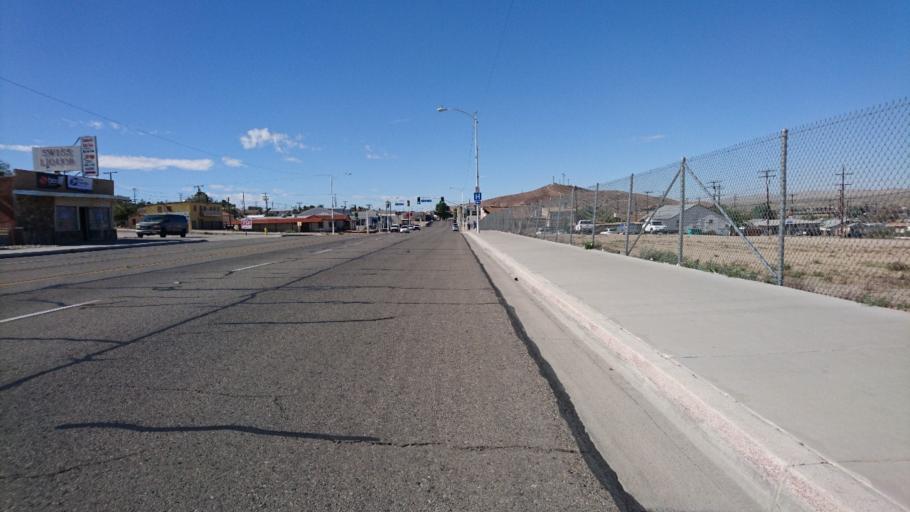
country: US
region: California
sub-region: San Bernardino County
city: Barstow
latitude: 34.8988
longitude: -117.0185
